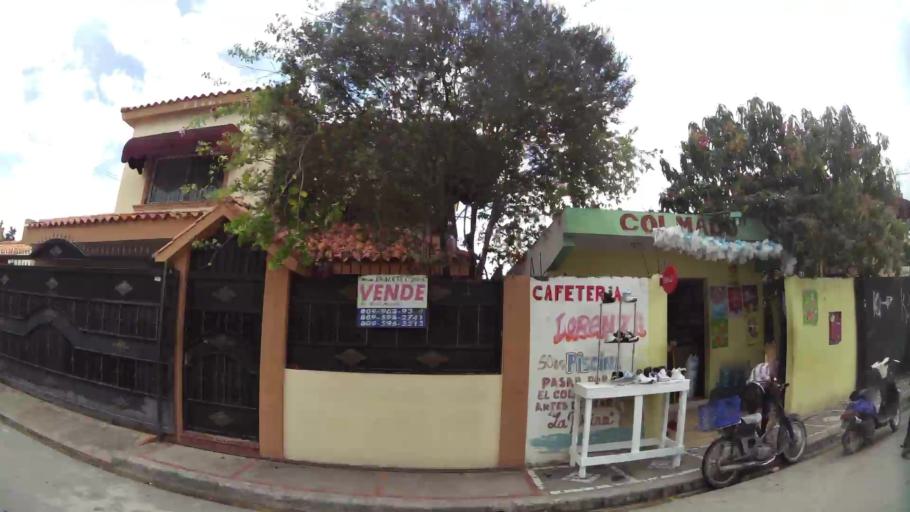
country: DO
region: Nacional
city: Ensanche Luperon
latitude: 18.5266
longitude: -69.8945
